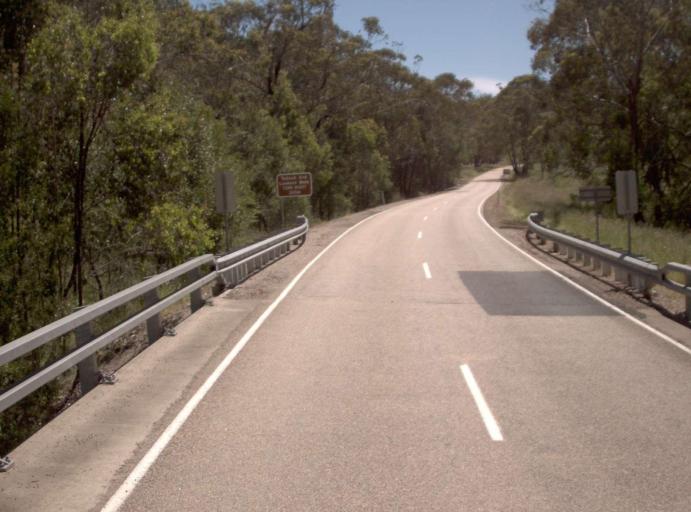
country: AU
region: Victoria
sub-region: East Gippsland
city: Lakes Entrance
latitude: -37.2323
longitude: 148.2600
